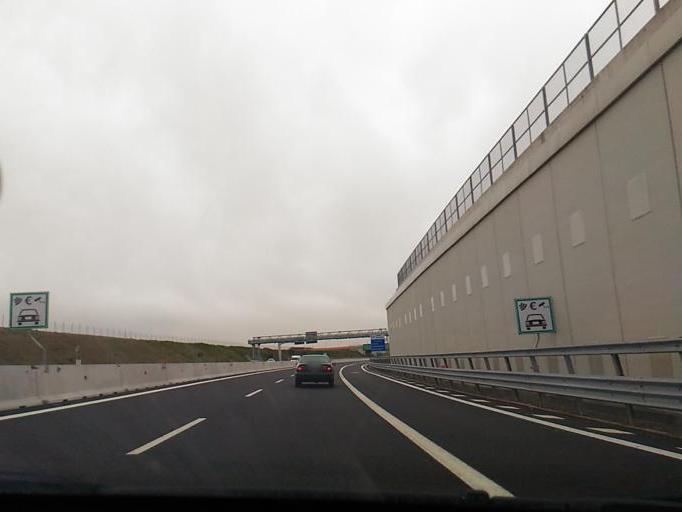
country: IT
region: Lombardy
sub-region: Provincia di Monza e Brianza
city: Lazzate
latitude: 45.6848
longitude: 9.0778
